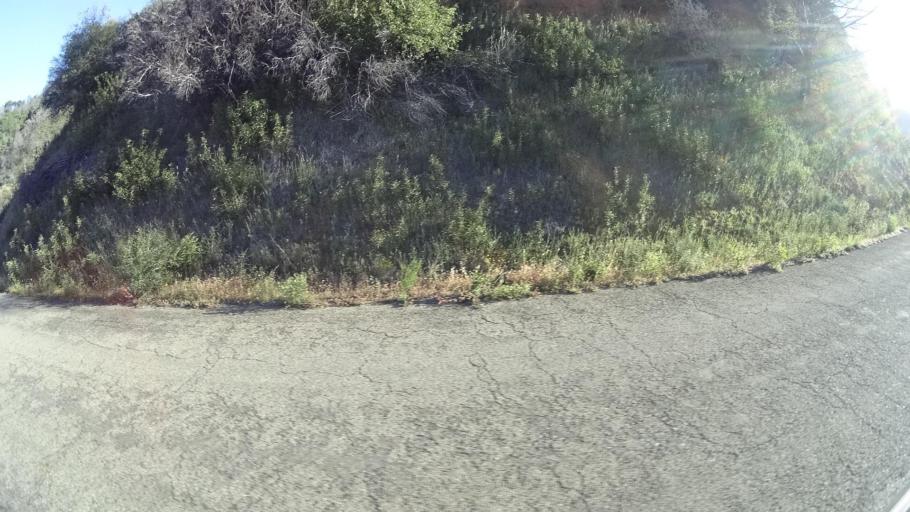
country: US
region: California
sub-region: Lake County
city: Upper Lake
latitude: 39.2579
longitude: -122.9448
